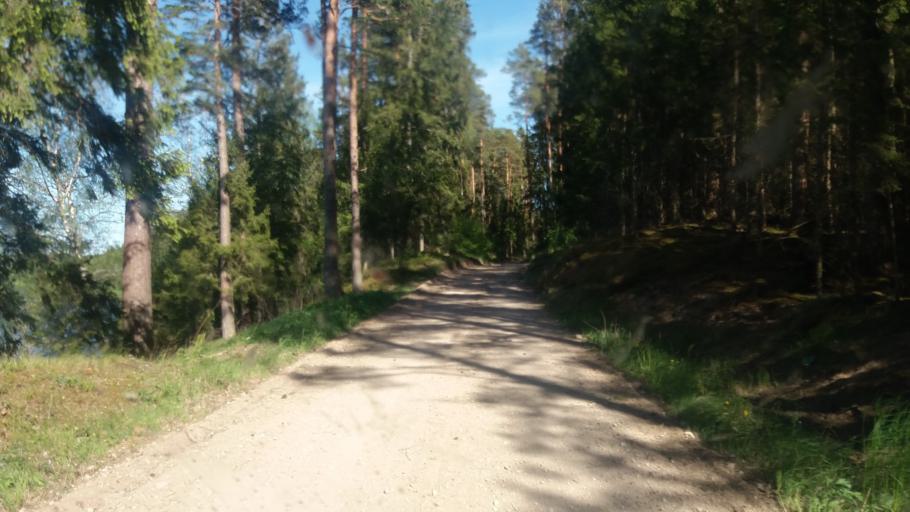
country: LV
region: Ventspils Rajons
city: Piltene
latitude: 57.0805
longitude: 21.7906
